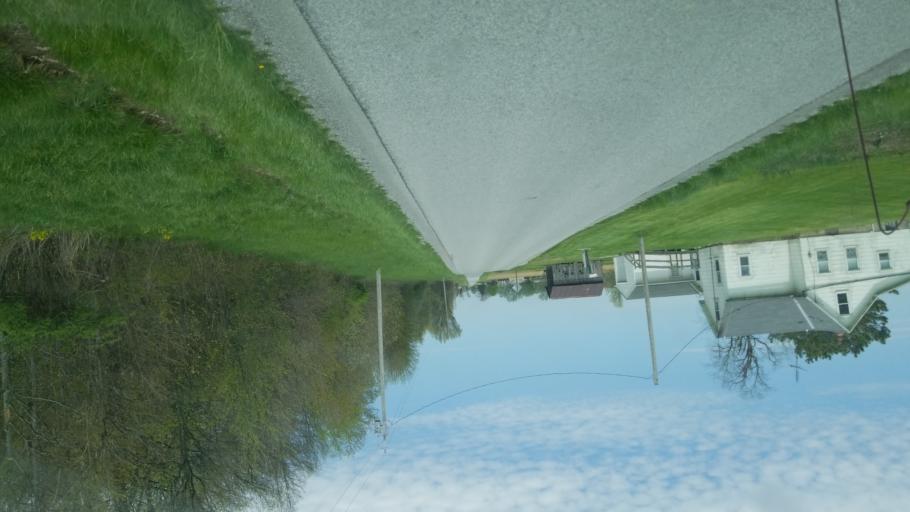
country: US
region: Ohio
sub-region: Hardin County
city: Ada
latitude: 40.7977
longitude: -83.8990
